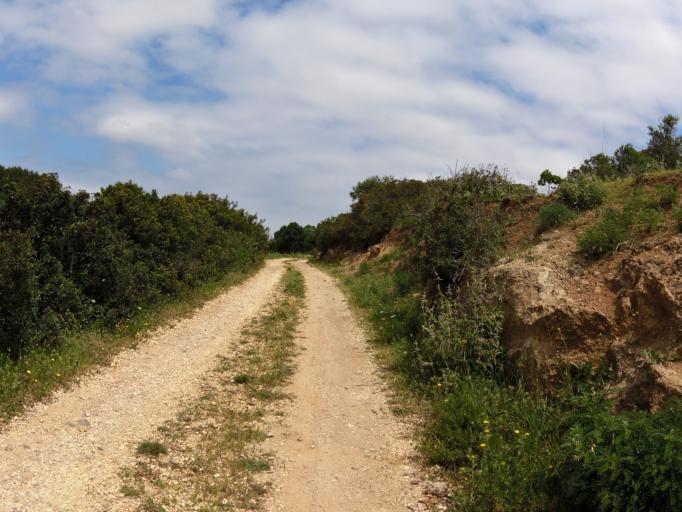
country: PT
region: Faro
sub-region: Vila do Bispo
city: Vila do Bispo
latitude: 37.0689
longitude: -8.8721
